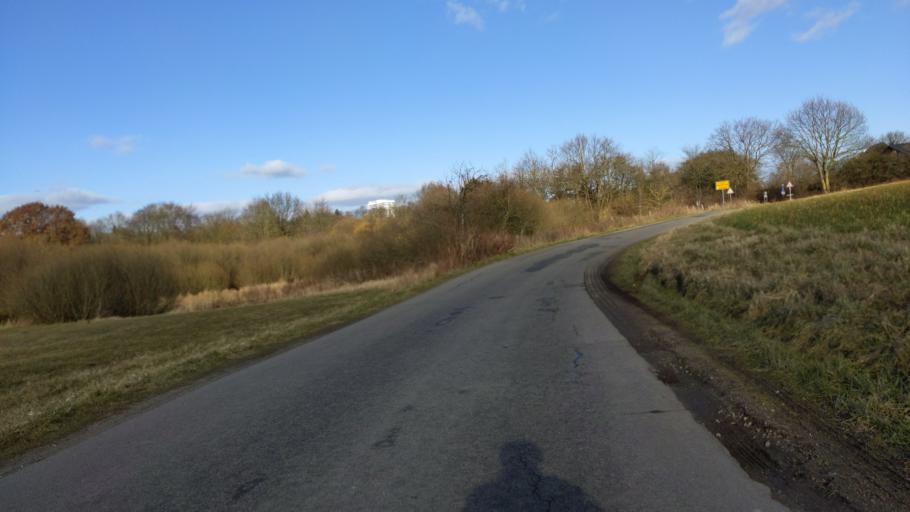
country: DE
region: Schleswig-Holstein
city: Timmendorfer Strand
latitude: 53.9961
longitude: 10.7597
